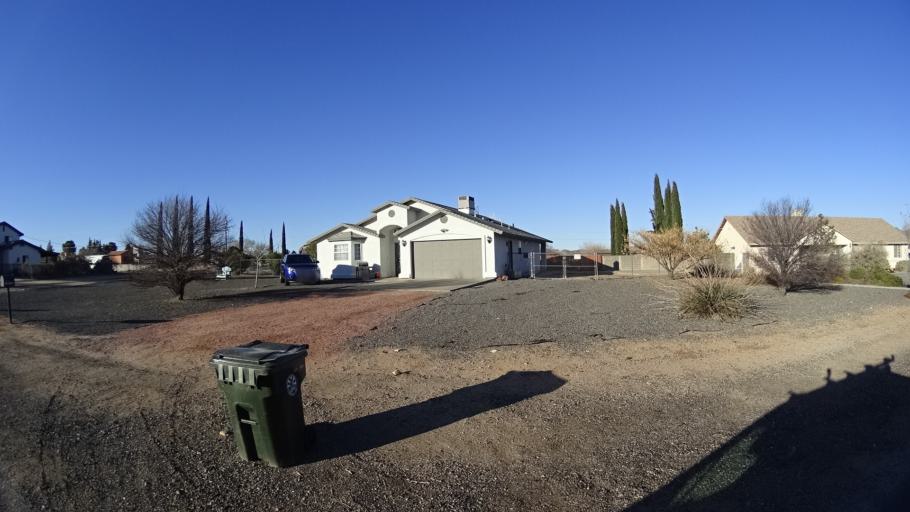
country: US
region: Arizona
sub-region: Mohave County
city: Kingman
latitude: 35.2065
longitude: -114.0095
